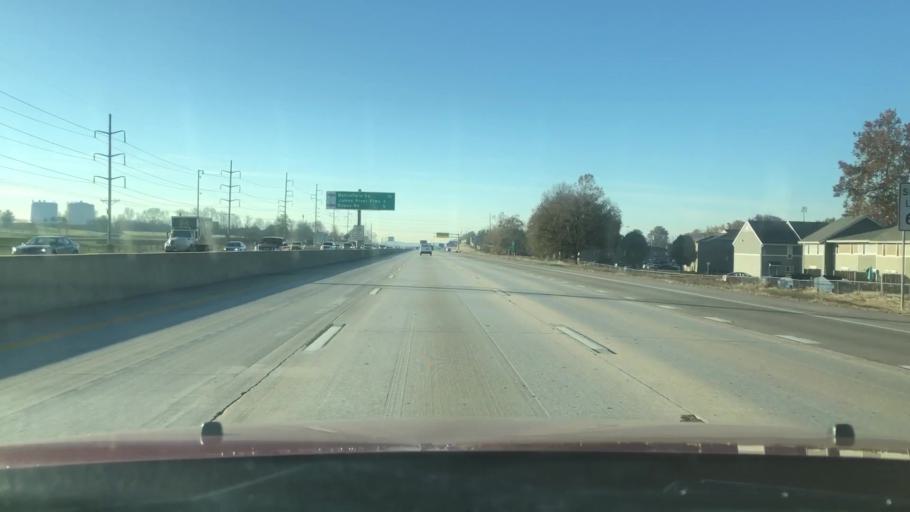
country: US
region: Missouri
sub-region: Greene County
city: Springfield
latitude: 37.1690
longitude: -93.2244
